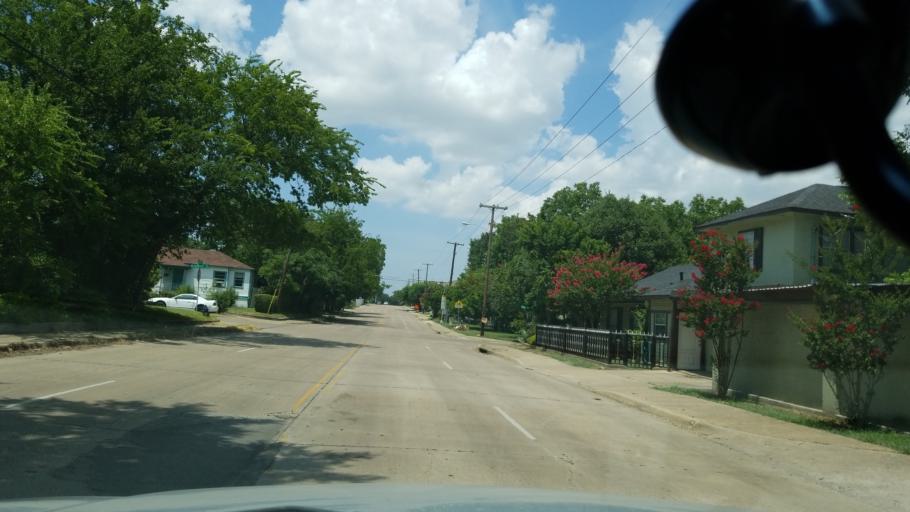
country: US
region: Texas
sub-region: Dallas County
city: Cockrell Hill
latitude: 32.7304
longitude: -96.8689
